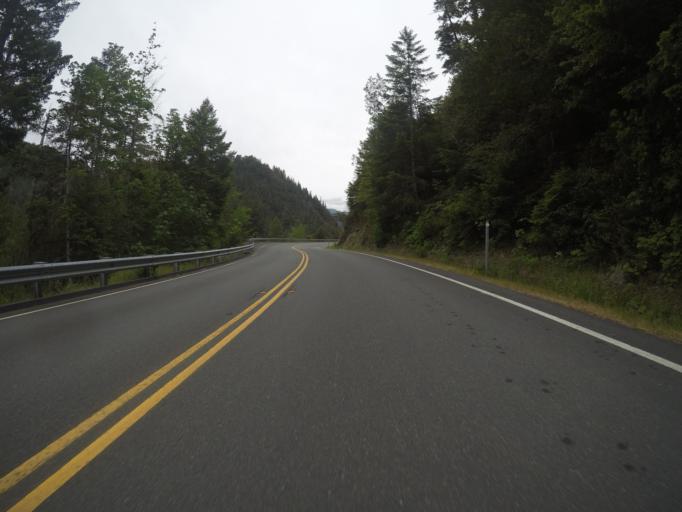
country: US
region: California
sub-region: Del Norte County
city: Bertsch-Oceanview
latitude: 41.7172
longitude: -123.9449
